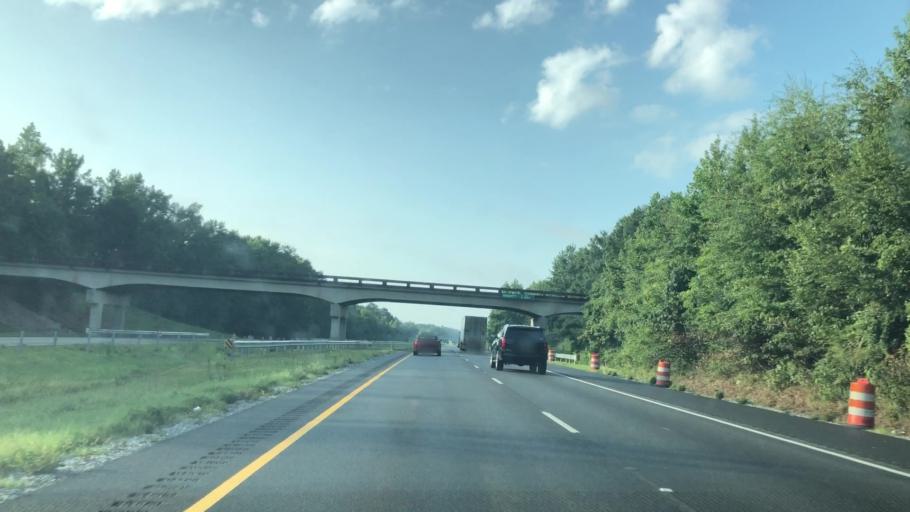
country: US
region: Alabama
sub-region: Chilton County
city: Clanton
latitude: 32.8509
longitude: -86.5982
